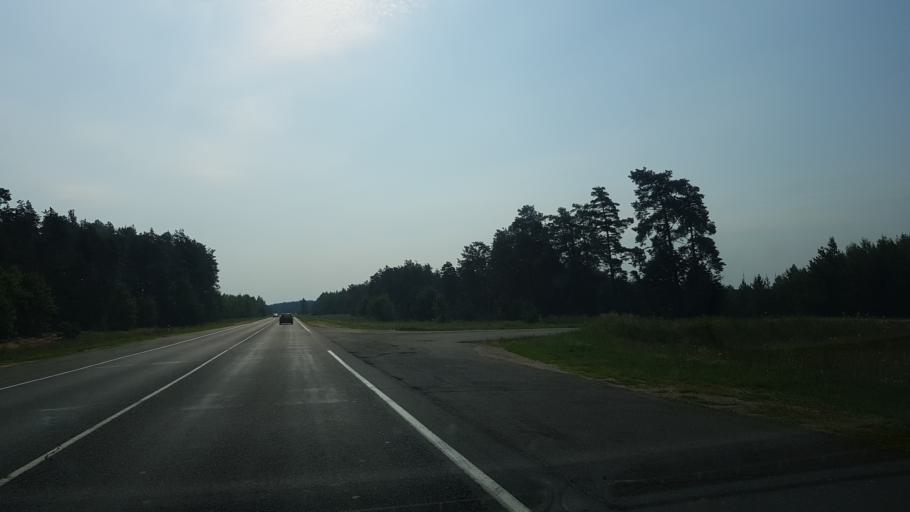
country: BY
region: Mogilev
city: Babruysk
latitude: 53.1654
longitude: 29.2898
